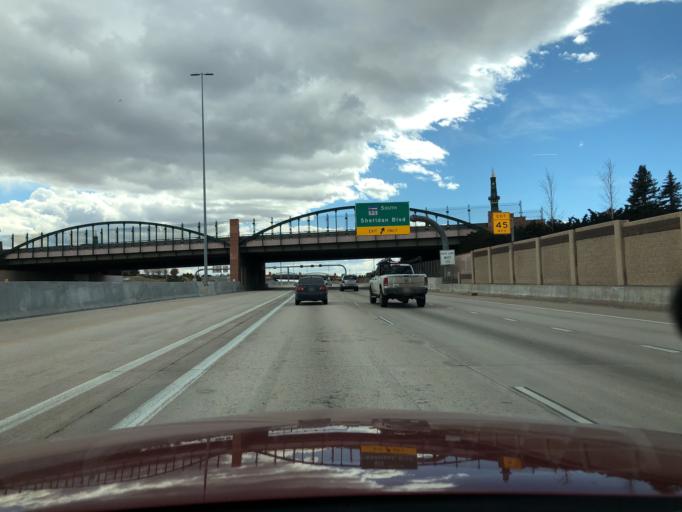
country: US
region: Colorado
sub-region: Adams County
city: Westminster
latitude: 39.8644
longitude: -105.0571
